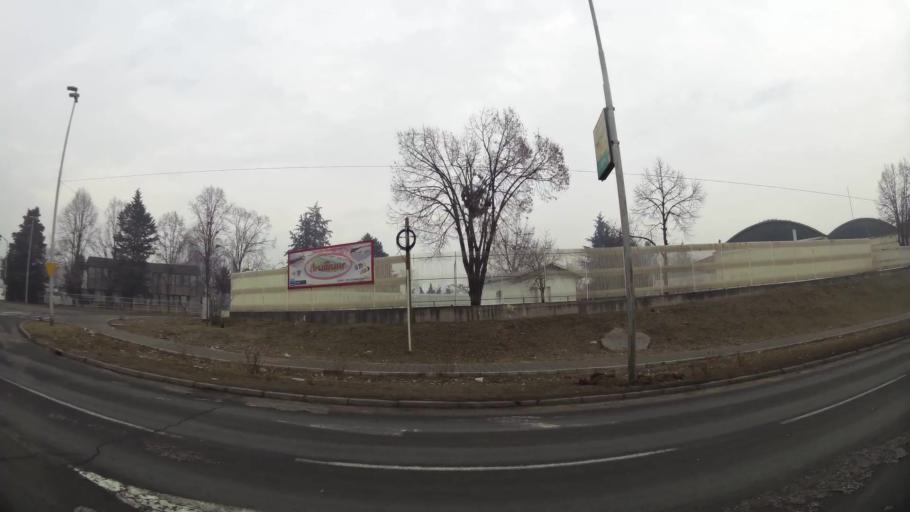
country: MK
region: Cair
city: Cair
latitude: 41.9994
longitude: 21.4731
